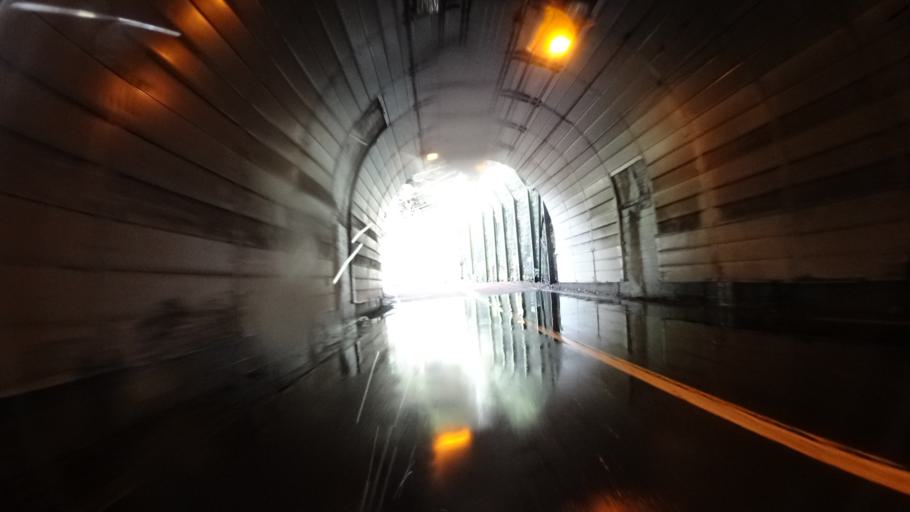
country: JP
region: Yamanashi
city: Uenohara
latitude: 35.7822
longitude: 139.0261
